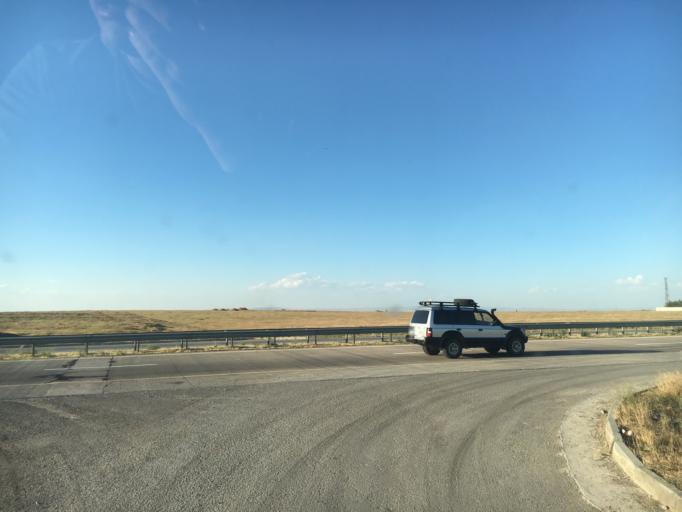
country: KZ
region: Ongtustik Qazaqstan
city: Shymkent
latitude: 42.4539
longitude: 69.6184
